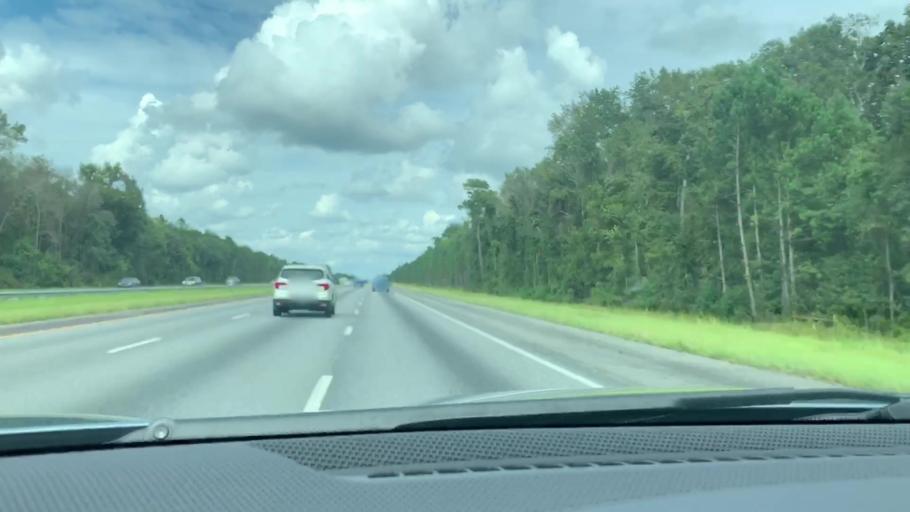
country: US
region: Georgia
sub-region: Liberty County
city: Midway
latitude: 31.6018
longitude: -81.4207
